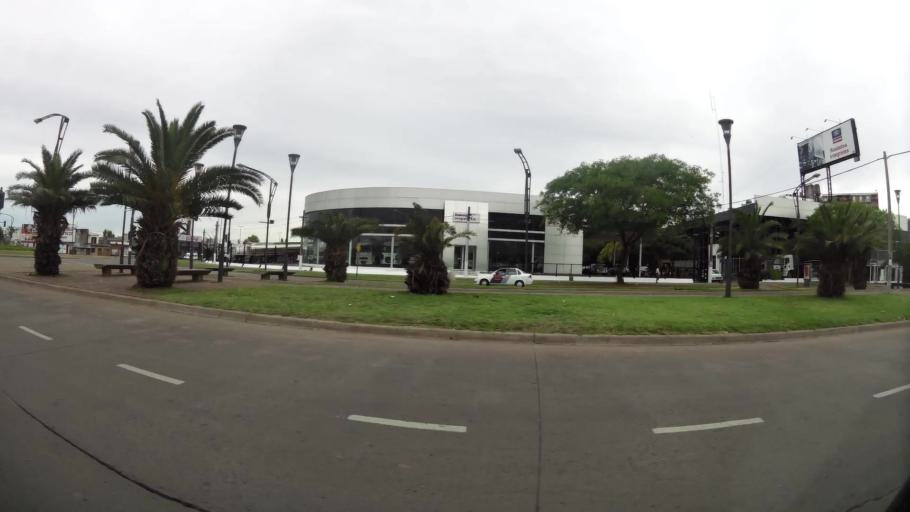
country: AR
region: Santa Fe
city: Gobernador Galvez
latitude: -32.9921
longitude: -60.6655
